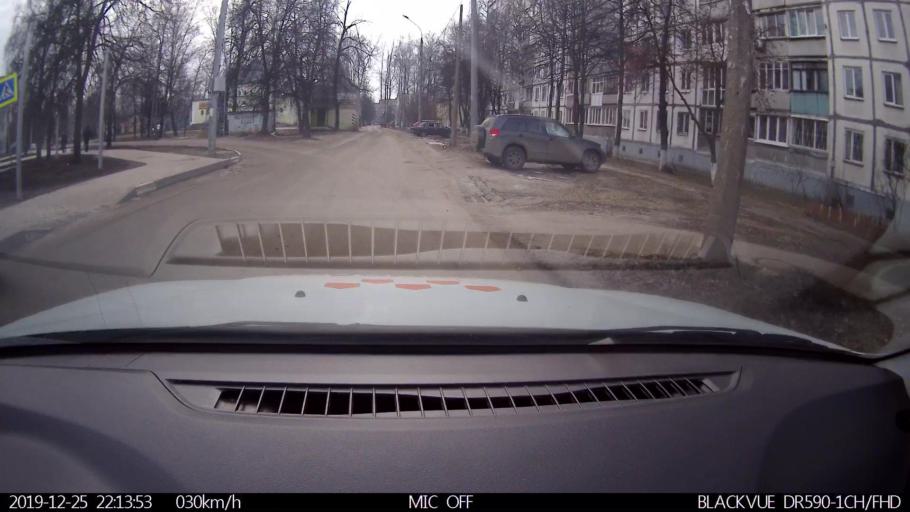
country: RU
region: Nizjnij Novgorod
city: Gorbatovka
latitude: 56.3332
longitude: 43.8466
